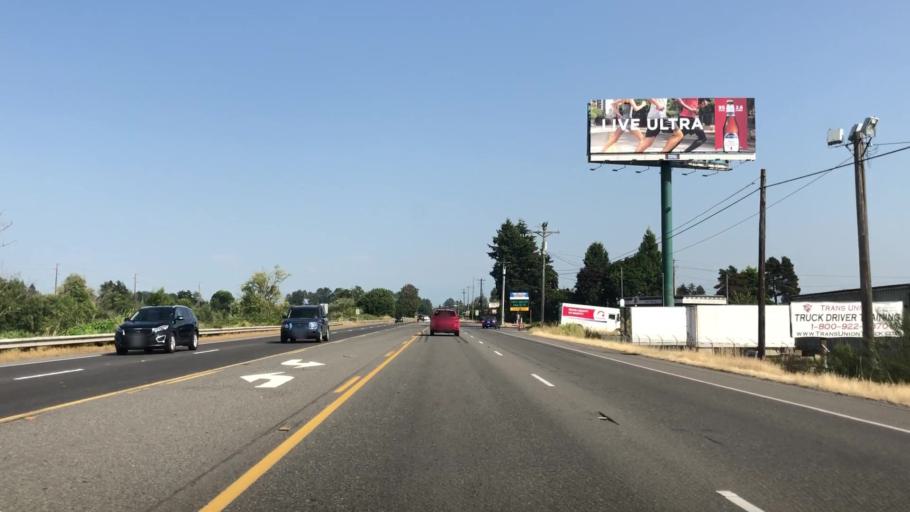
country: US
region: Washington
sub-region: Pierce County
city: Fife
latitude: 47.2257
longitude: -122.3667
